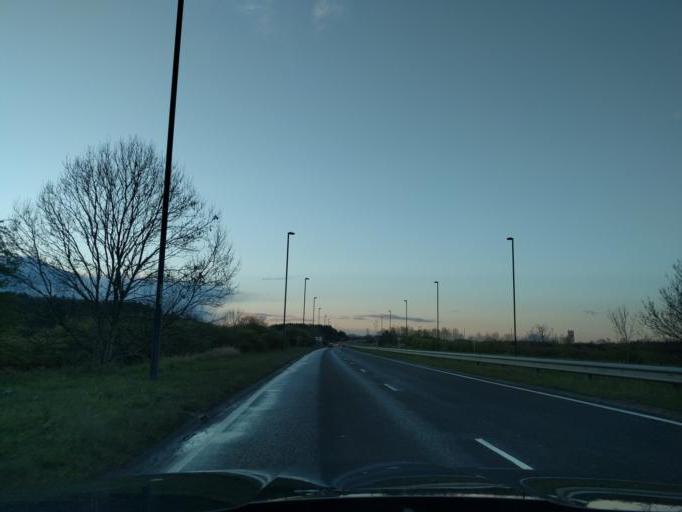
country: GB
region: England
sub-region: Newcastle upon Tyne
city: Gosforth
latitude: 55.0365
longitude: -1.5922
